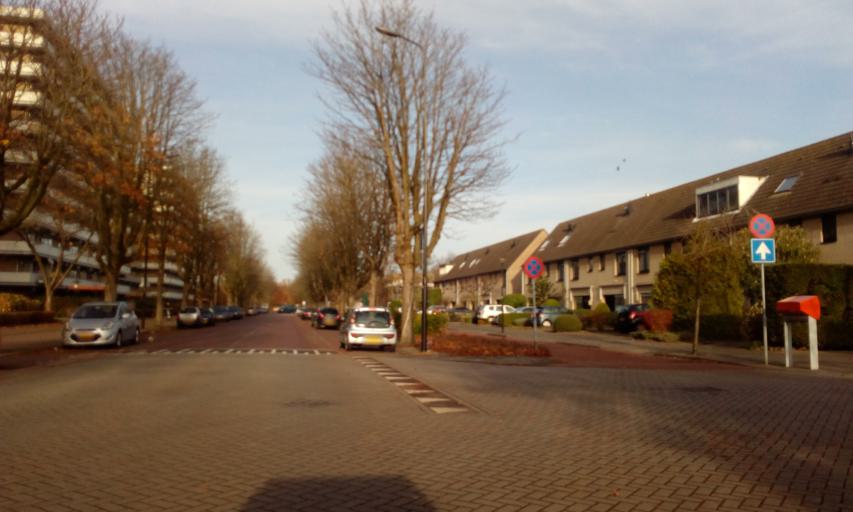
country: NL
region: South Holland
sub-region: Gemeente Rijswijk
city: Rijswijk
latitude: 52.0416
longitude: 4.3129
